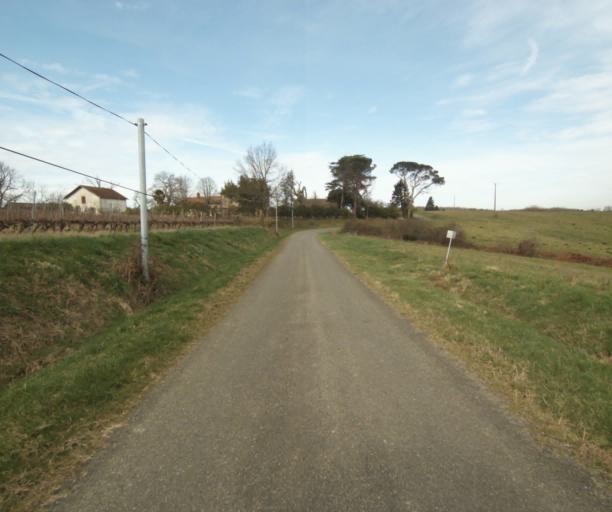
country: FR
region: Aquitaine
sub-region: Departement des Landes
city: Gabarret
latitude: 43.9102
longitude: 0.0362
